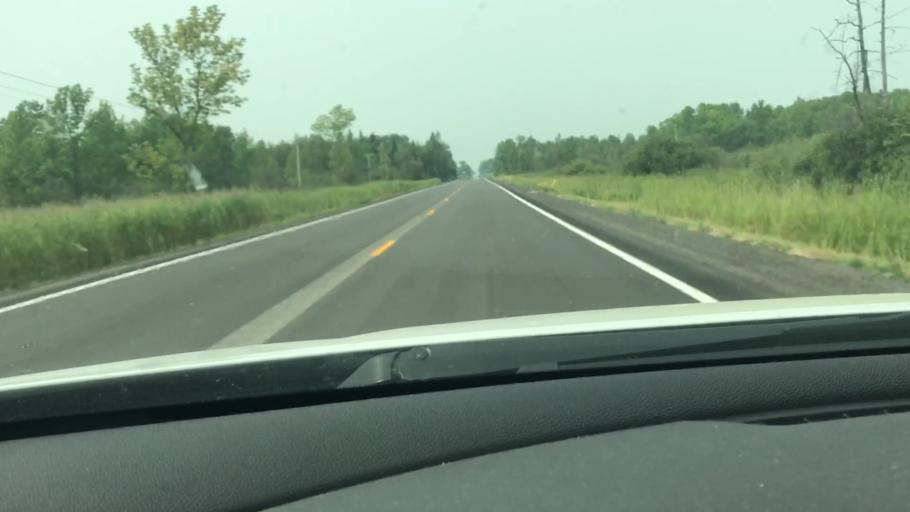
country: US
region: Minnesota
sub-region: Itasca County
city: Cohasset
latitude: 47.3520
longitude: -93.8418
